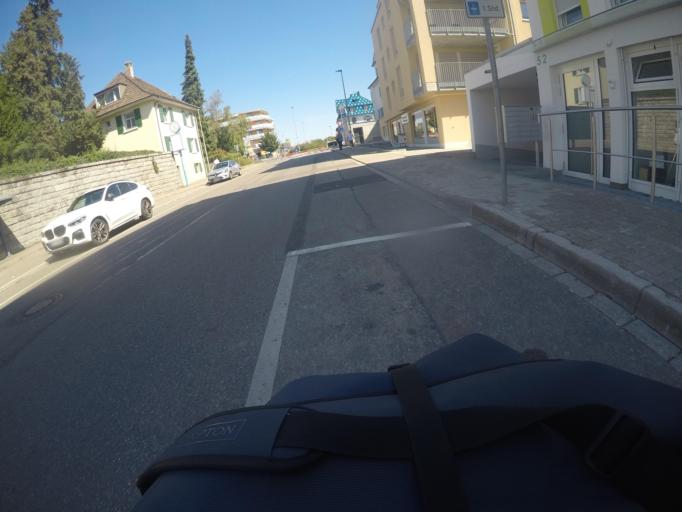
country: DE
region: Baden-Wuerttemberg
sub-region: Freiburg Region
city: Bad Krozingen
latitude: 47.9179
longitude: 7.7022
